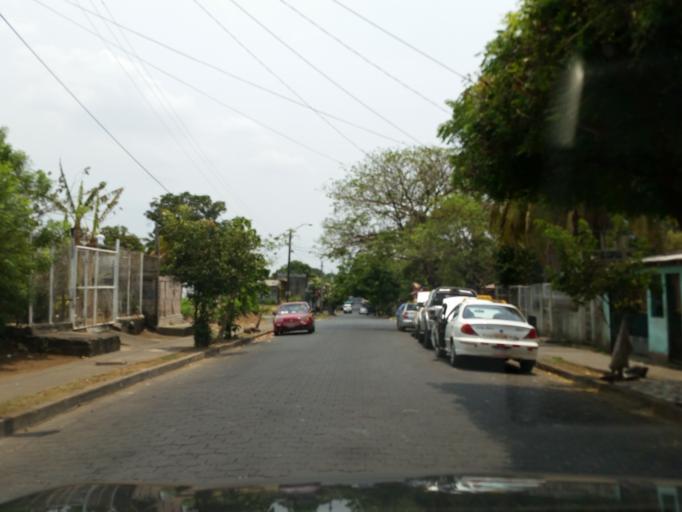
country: NI
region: Managua
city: Managua
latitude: 12.1358
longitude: -86.2387
